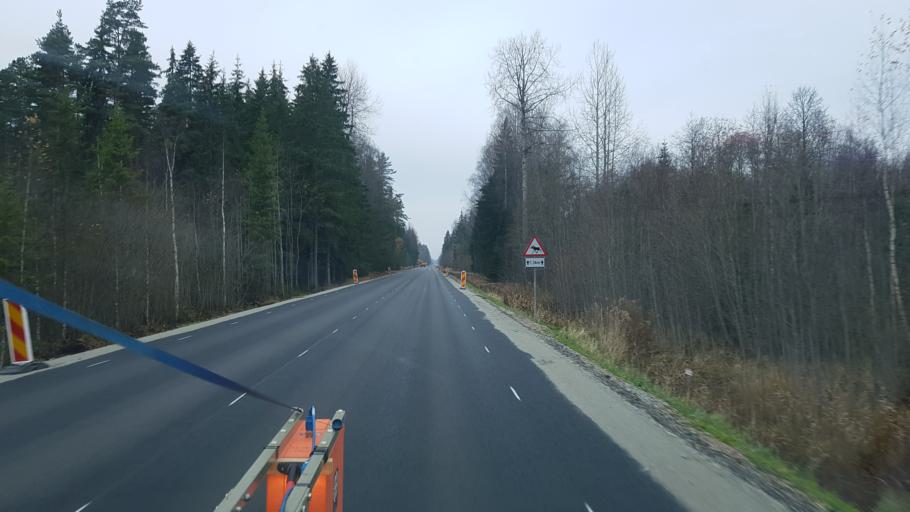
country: EE
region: Paernumaa
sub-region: Vaendra vald (alev)
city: Vandra
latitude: 58.8291
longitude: 25.1096
